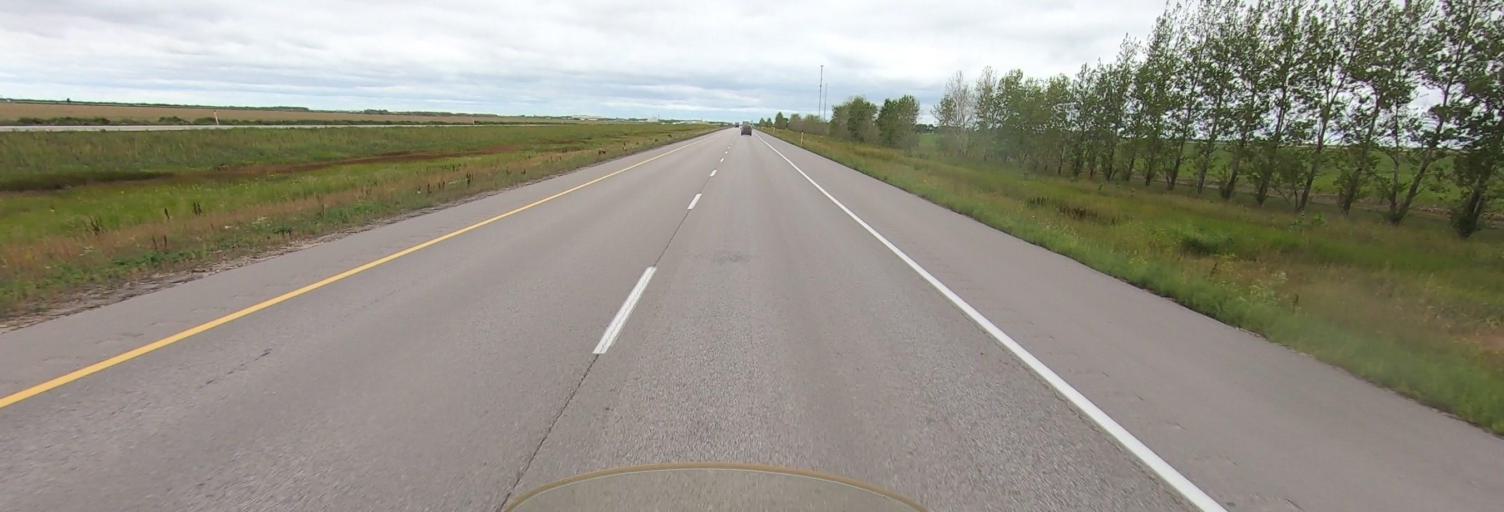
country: CA
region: Manitoba
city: Headingley
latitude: 49.8954
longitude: -97.6952
